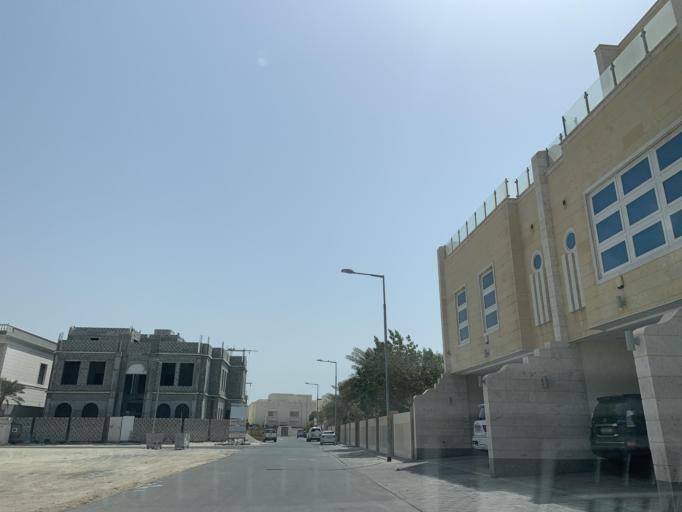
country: BH
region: Manama
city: Manama
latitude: 26.2009
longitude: 50.5685
